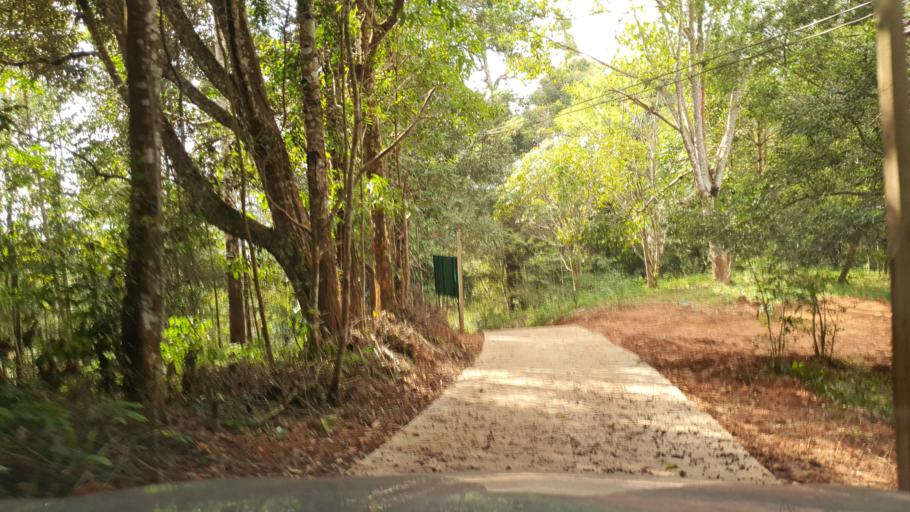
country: TH
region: Chiang Mai
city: Mae On
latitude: 18.9537
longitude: 99.2983
